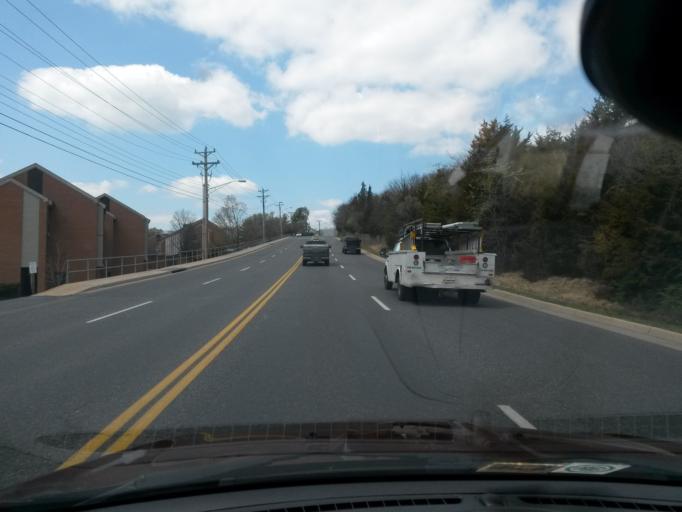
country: US
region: Virginia
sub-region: City of Harrisonburg
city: Harrisonburg
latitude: 38.4386
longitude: -78.8656
